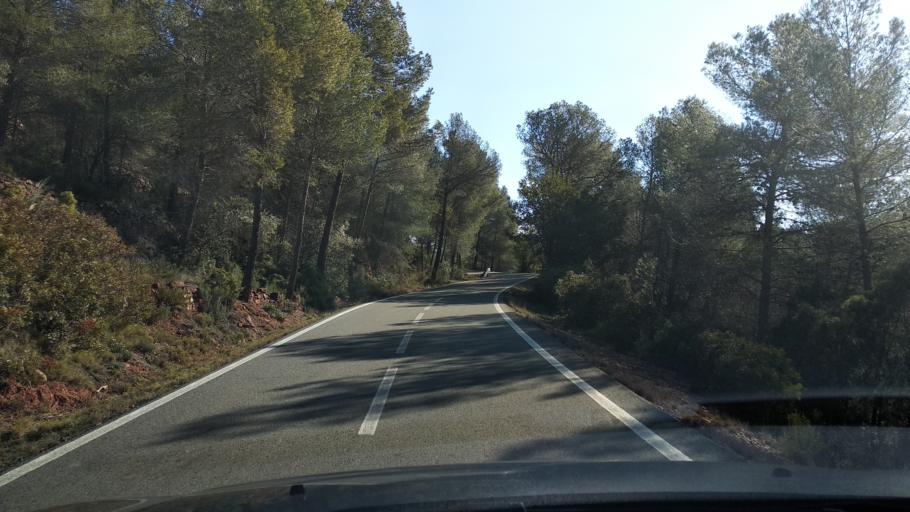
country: ES
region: Catalonia
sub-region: Provincia de Tarragona
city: el Masroig
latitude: 41.1714
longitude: 0.7093
